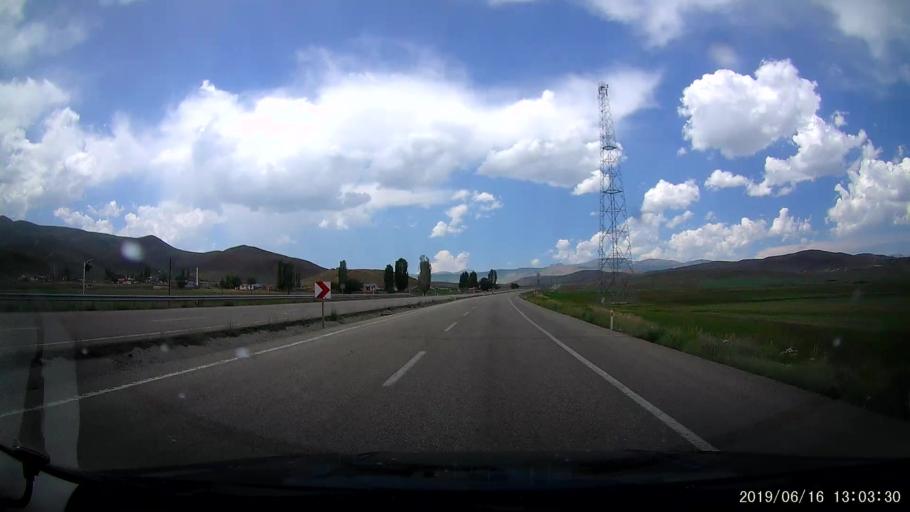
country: TR
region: Agri
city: Sulucem
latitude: 39.5820
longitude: 43.7890
